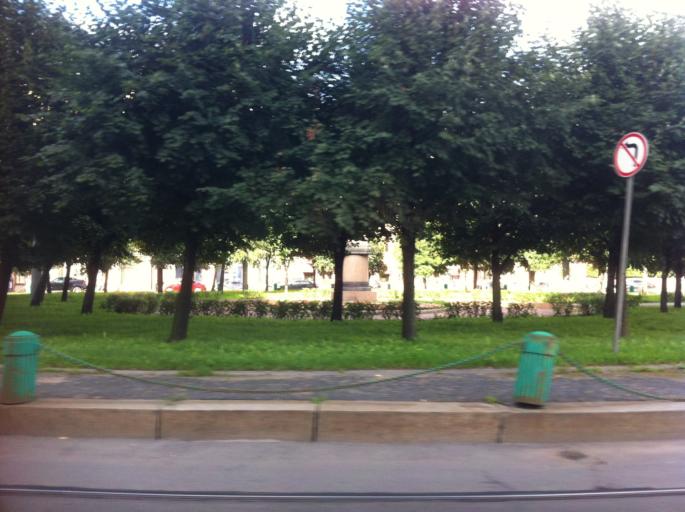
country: RU
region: St.-Petersburg
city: Admiralteisky
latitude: 59.9014
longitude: 30.2728
